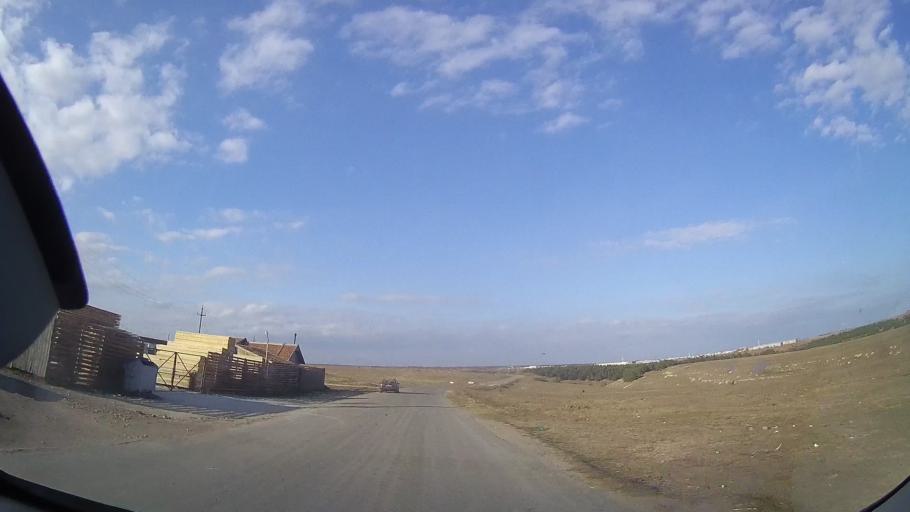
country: RO
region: Constanta
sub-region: Comuna Limanu
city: Limanu
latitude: 43.8044
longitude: 28.5208
